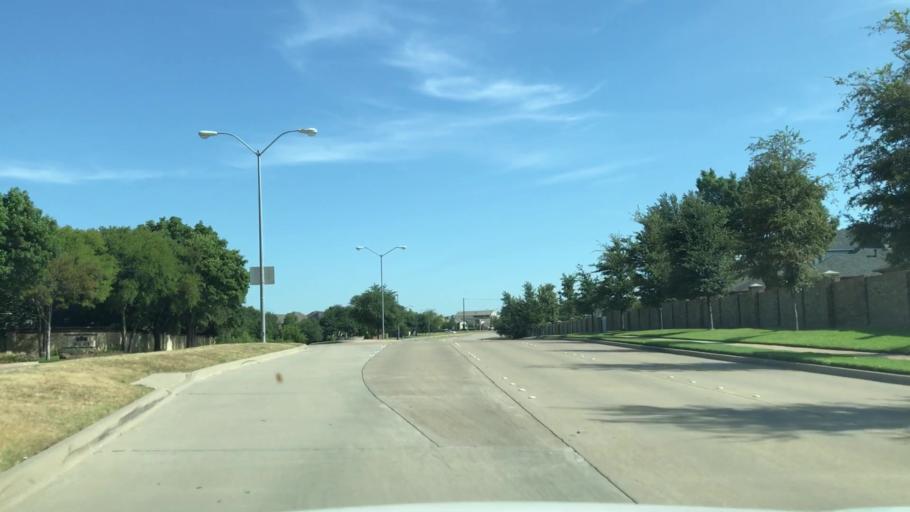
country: US
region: Texas
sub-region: Denton County
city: The Colony
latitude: 33.0636
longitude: -96.8394
